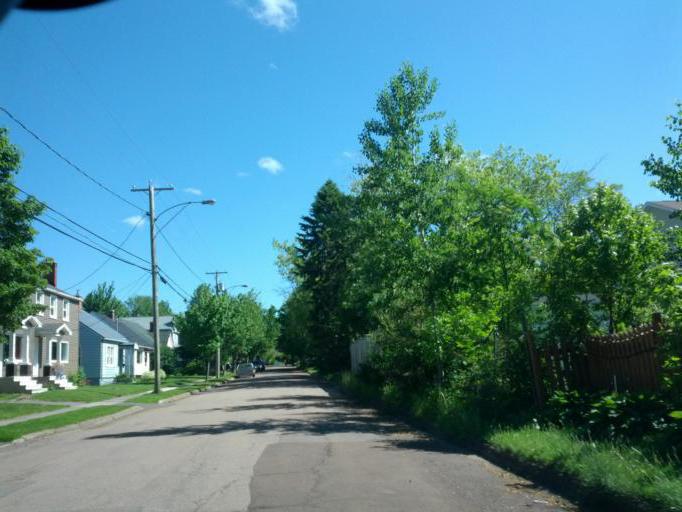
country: CA
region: New Brunswick
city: Moncton
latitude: 46.1004
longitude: -64.7928
